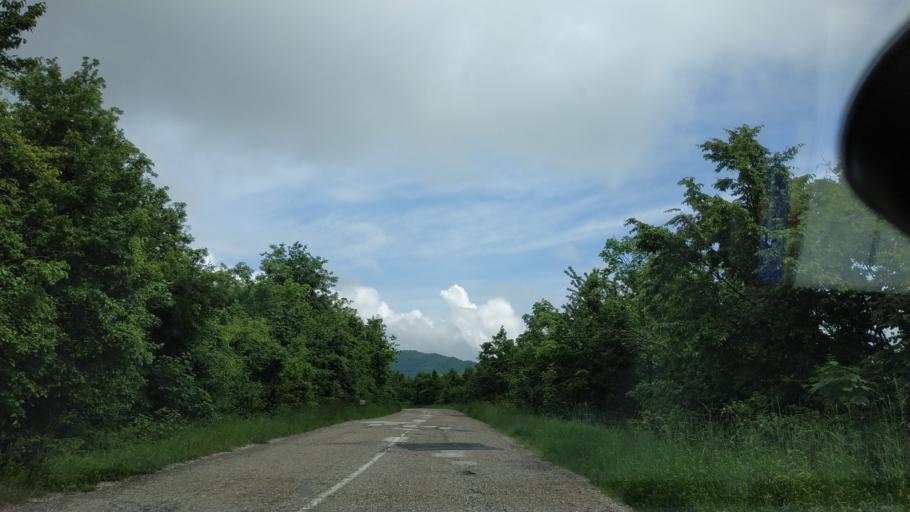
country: RS
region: Central Serbia
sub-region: Zajecarski Okrug
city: Boljevac
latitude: 43.7231
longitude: 21.9524
